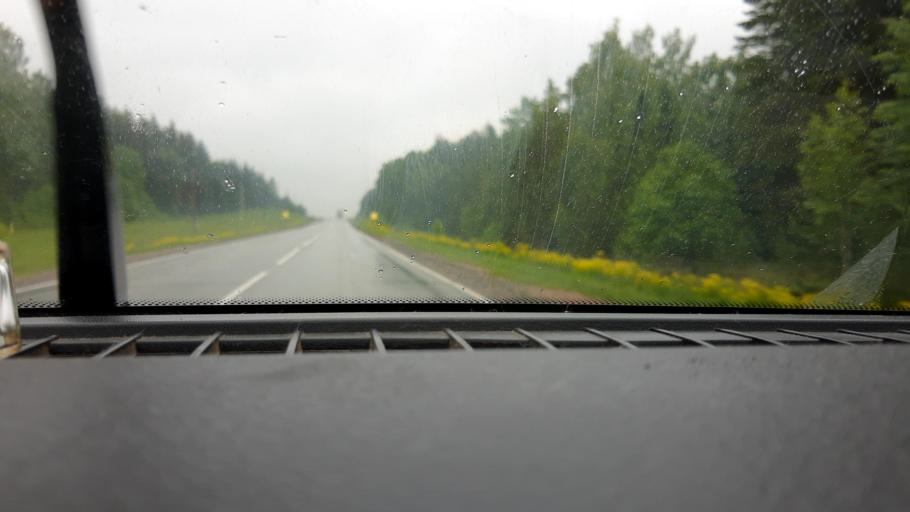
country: RU
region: Bashkortostan
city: Belebey
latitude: 54.2142
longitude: 54.0762
